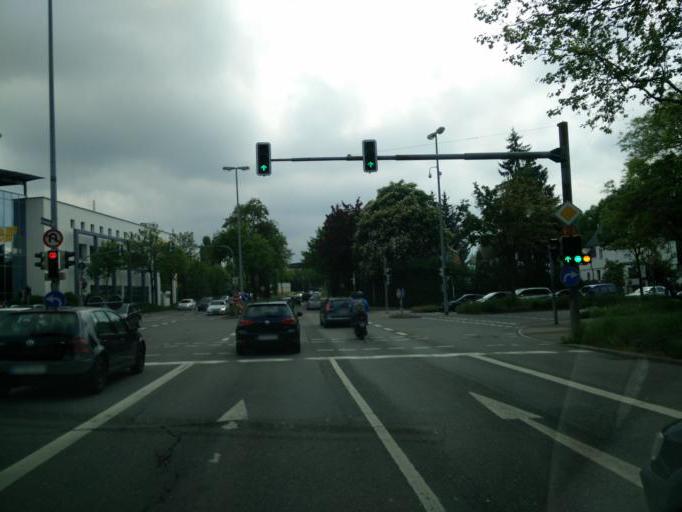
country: DE
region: Baden-Wuerttemberg
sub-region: Tuebingen Region
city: Reutlingen
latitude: 48.4986
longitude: 9.1973
